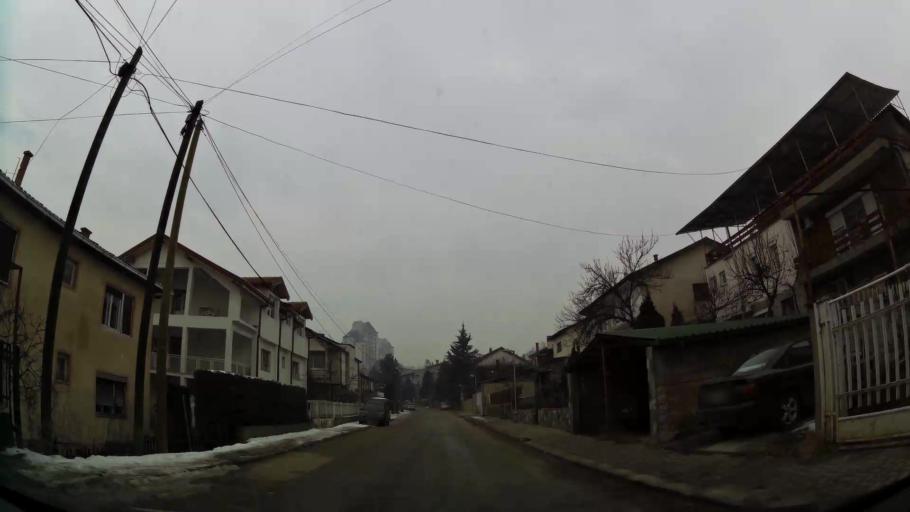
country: MK
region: Cair
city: Cair
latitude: 42.0138
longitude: 21.4560
